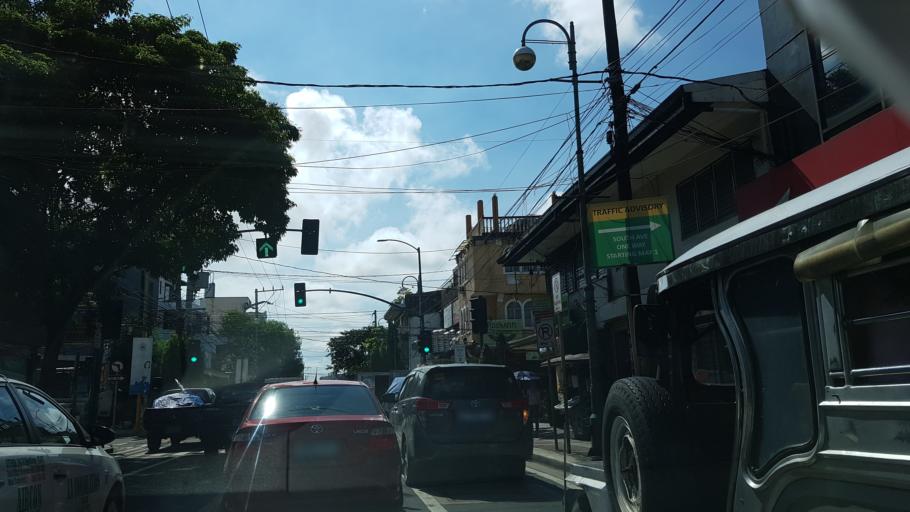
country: PH
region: Metro Manila
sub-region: Mandaluyong
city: Mandaluyong City
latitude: 14.5711
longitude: 121.0194
